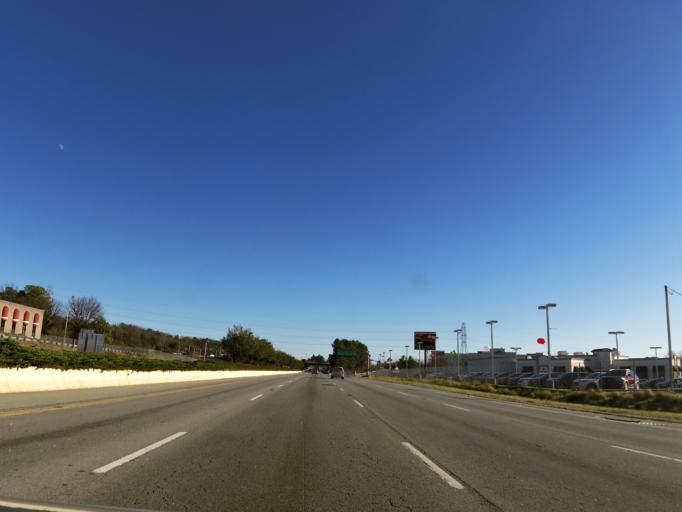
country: US
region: South Carolina
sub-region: Greenville County
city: Wade Hampton
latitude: 34.8426
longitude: -82.3180
